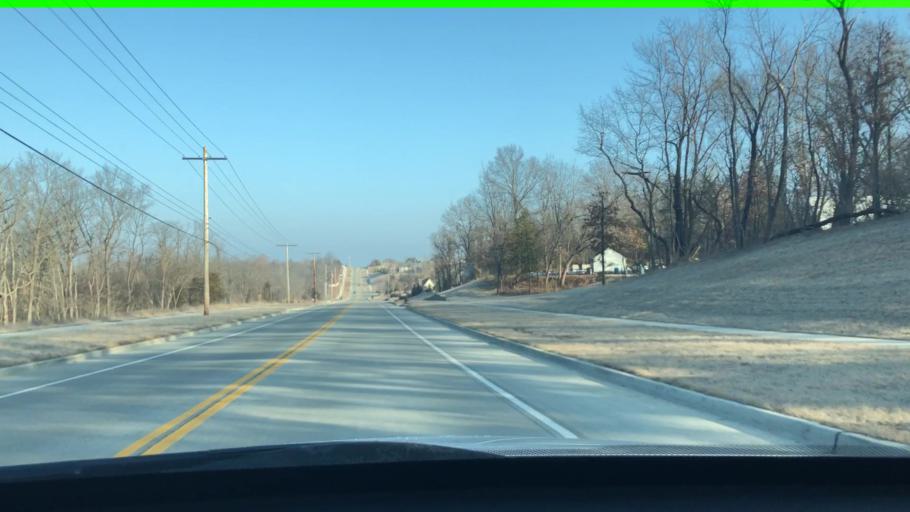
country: US
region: Missouri
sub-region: Boone County
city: Columbia
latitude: 38.9006
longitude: -92.4006
